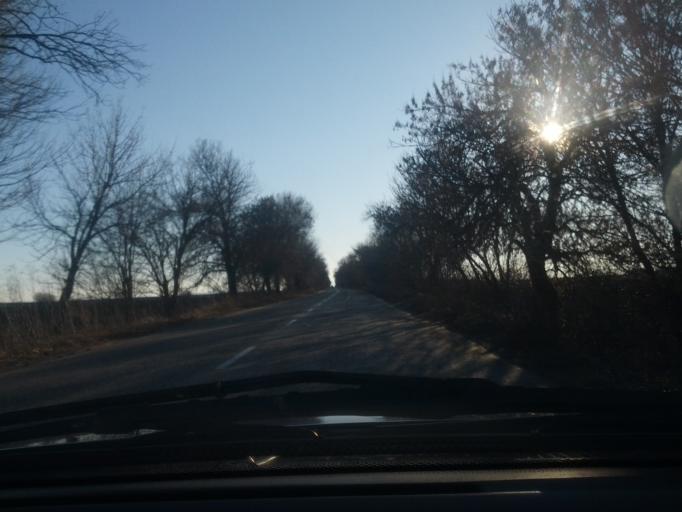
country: BG
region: Vratsa
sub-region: Obshtina Miziya
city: Miziya
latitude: 43.5712
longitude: 23.8120
